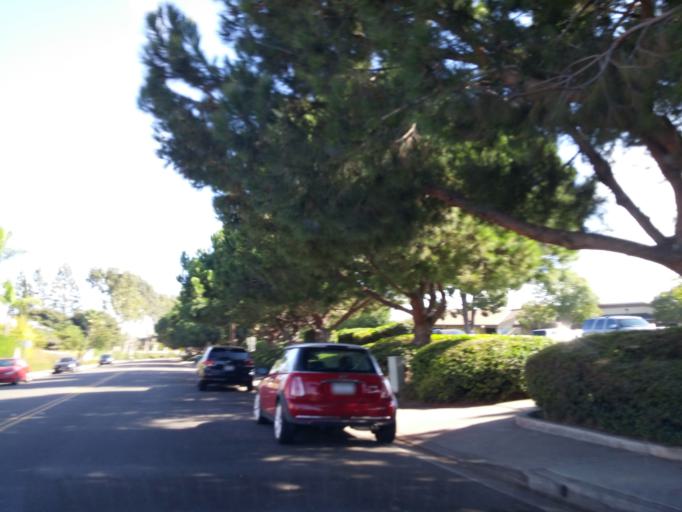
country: US
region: California
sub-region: Orange County
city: Irvine
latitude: 33.6798
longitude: -117.7925
